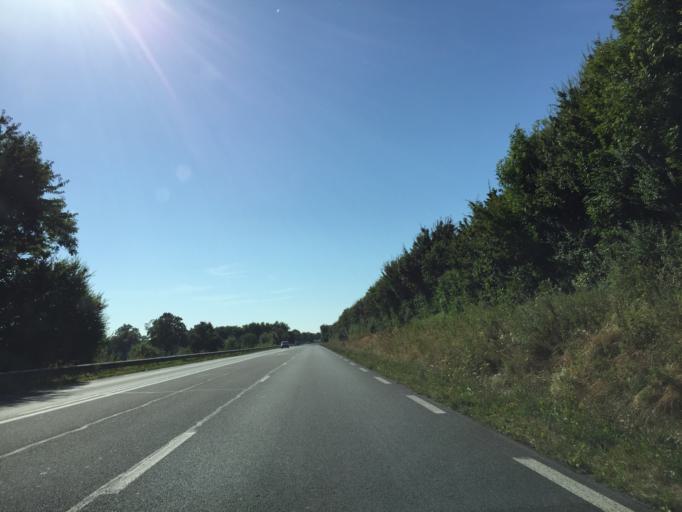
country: FR
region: Lower Normandy
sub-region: Departement du Calvados
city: Lisieux
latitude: 49.1557
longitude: 0.2423
